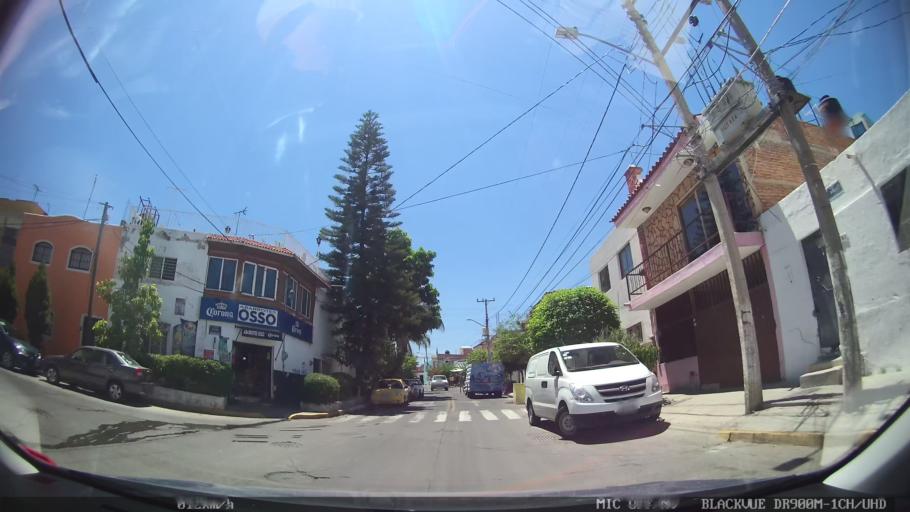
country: MX
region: Jalisco
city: Tlaquepaque
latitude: 20.6710
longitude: -103.2711
